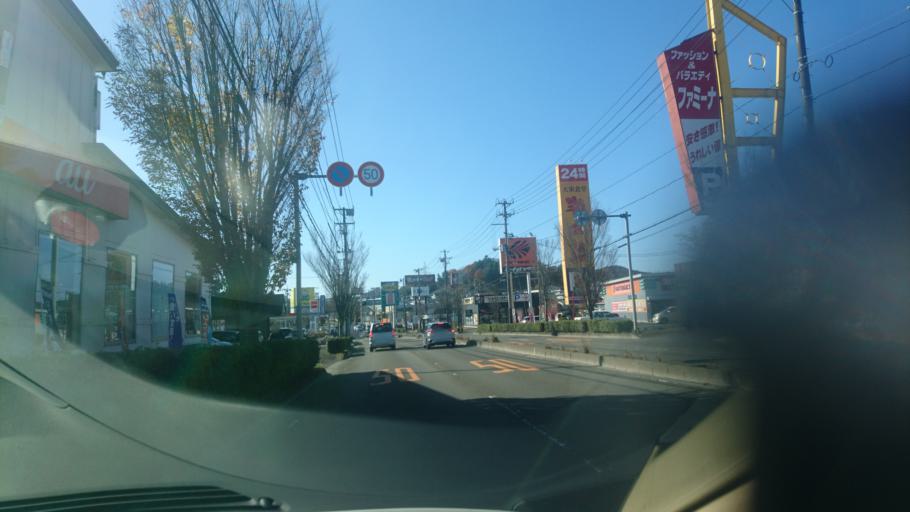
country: JP
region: Miyagi
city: Sendai-shi
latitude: 38.2939
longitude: 140.8235
